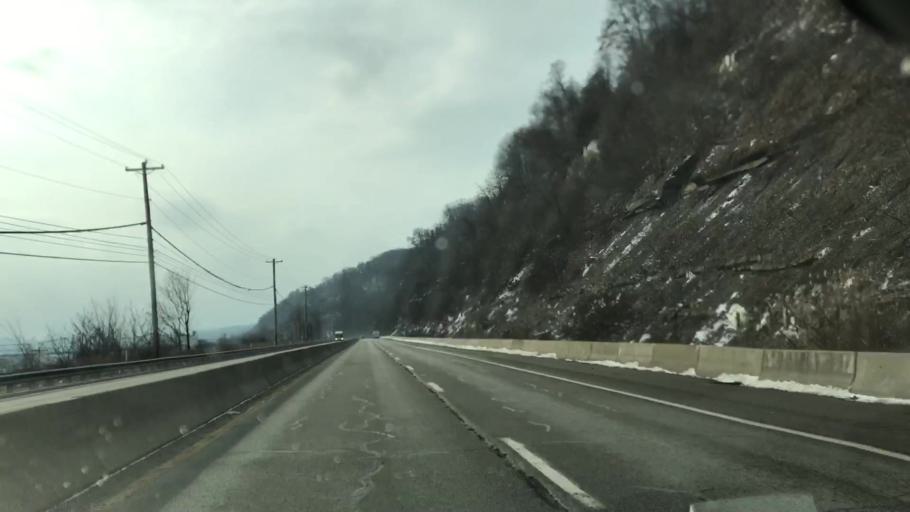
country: US
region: Pennsylvania
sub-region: Beaver County
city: Economy
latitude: 40.6024
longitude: -80.2420
